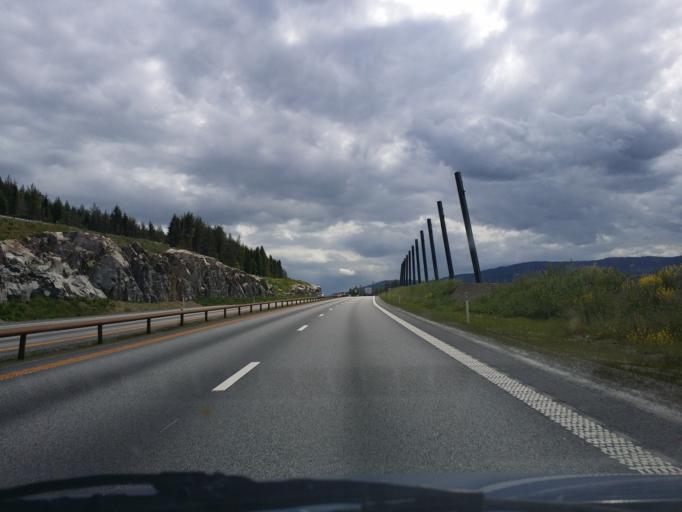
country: NO
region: Hedmark
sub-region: Stange
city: Stange
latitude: 60.5397
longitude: 11.2455
